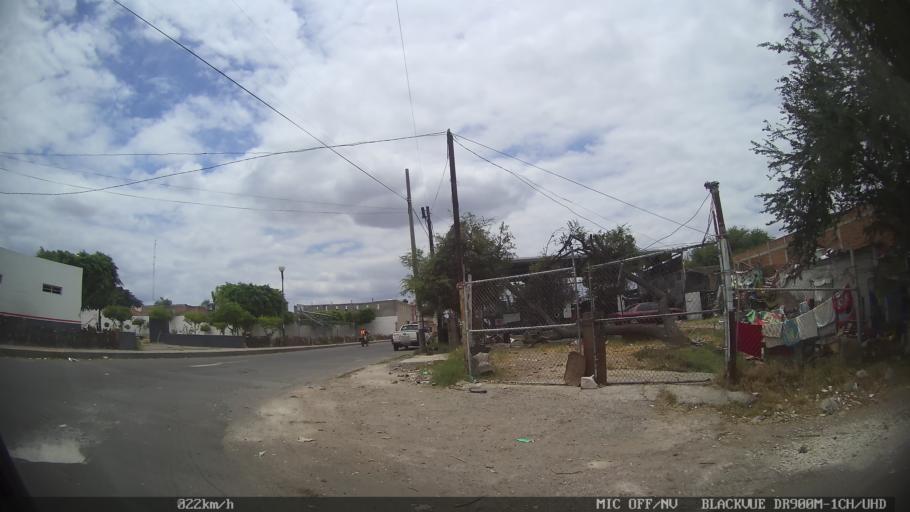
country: MX
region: Jalisco
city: Tlaquepaque
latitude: 20.6452
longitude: -103.2633
